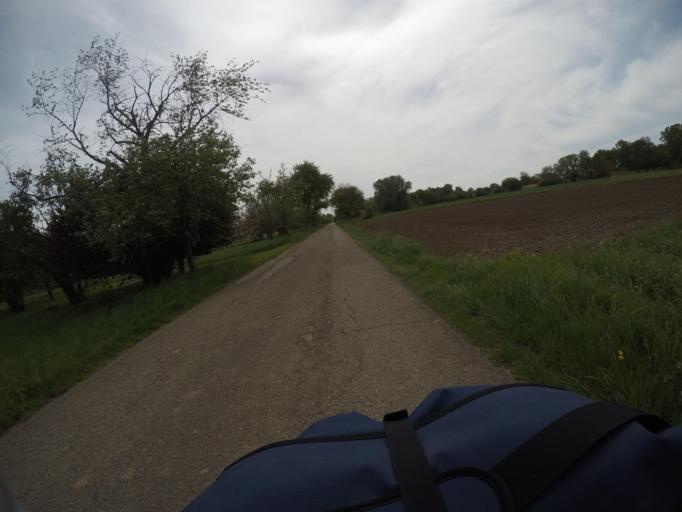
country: DE
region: Baden-Wuerttemberg
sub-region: Freiburg Region
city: Kehl
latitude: 48.5948
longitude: 7.8411
